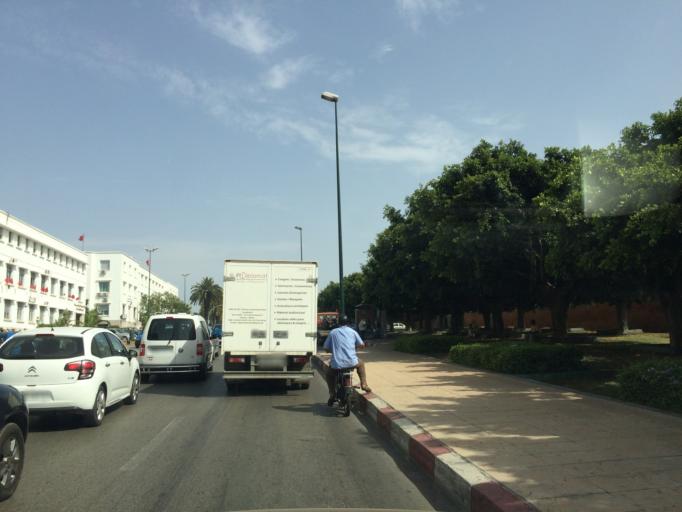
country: MA
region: Rabat-Sale-Zemmour-Zaer
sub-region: Rabat
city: Rabat
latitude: 34.0082
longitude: -6.8288
